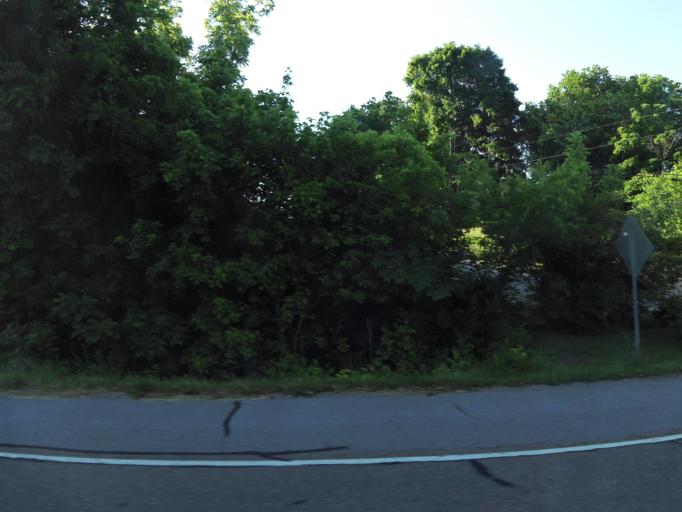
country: US
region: Tennessee
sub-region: Sevier County
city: Sevierville
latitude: 35.8533
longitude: -83.6349
